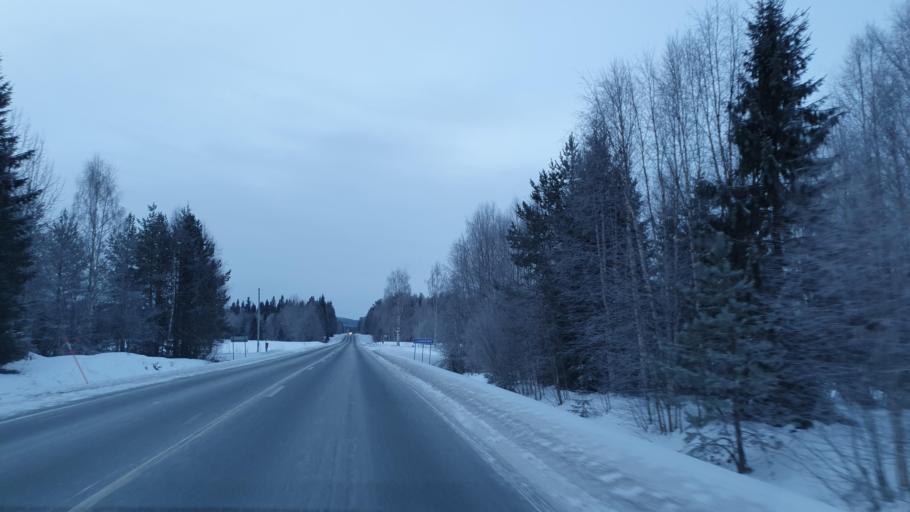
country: FI
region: Lapland
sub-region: Torniolaakso
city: Pello
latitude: 66.6083
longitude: 23.8874
